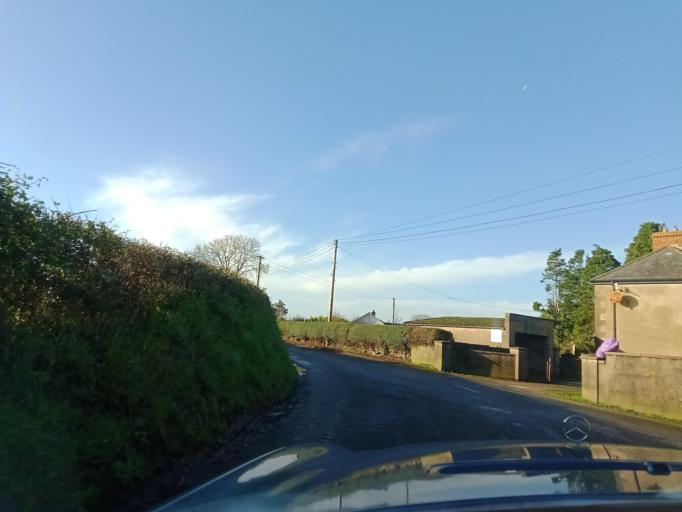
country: IE
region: Leinster
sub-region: Kilkenny
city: Mooncoin
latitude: 52.3001
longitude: -7.2185
